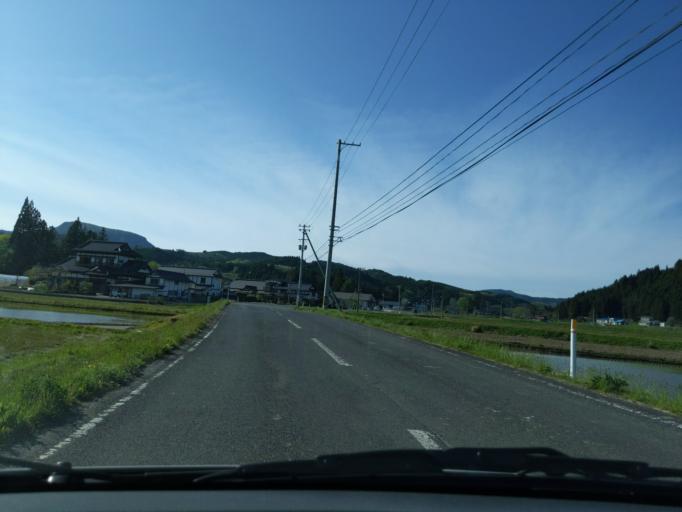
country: JP
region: Iwate
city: Ichinoseki
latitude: 38.8389
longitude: 140.9098
